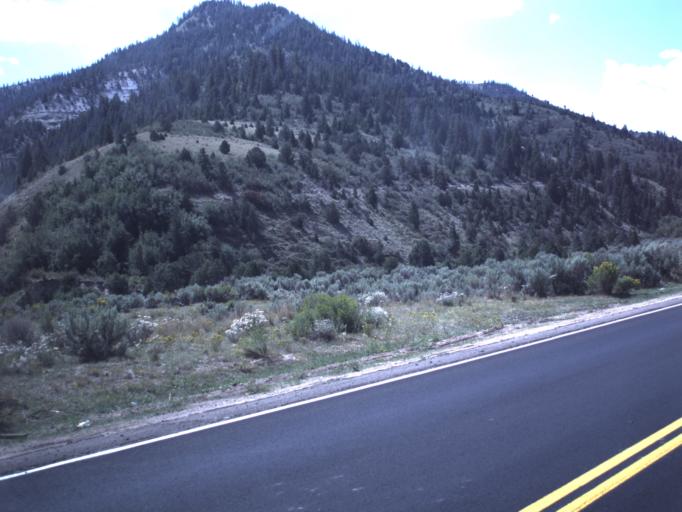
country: US
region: Utah
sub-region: Duchesne County
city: Duchesne
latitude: 39.9523
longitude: -110.6531
